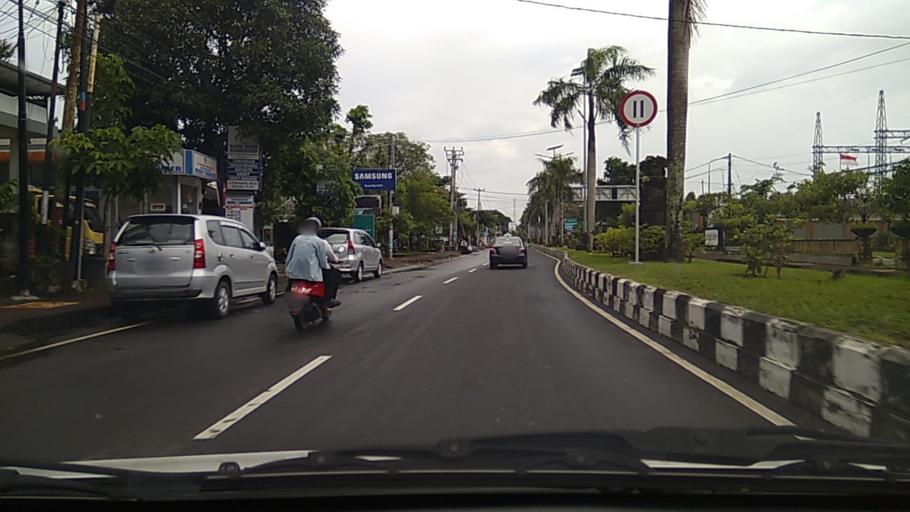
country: ID
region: Bali
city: Bualu
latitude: -8.7983
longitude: 115.2226
